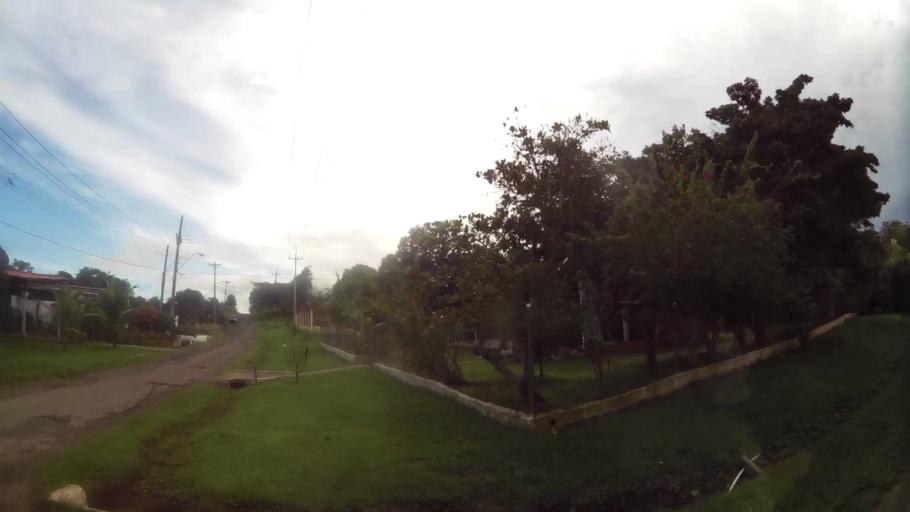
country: PA
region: Panama
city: El Coco
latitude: 8.8652
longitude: -79.8079
